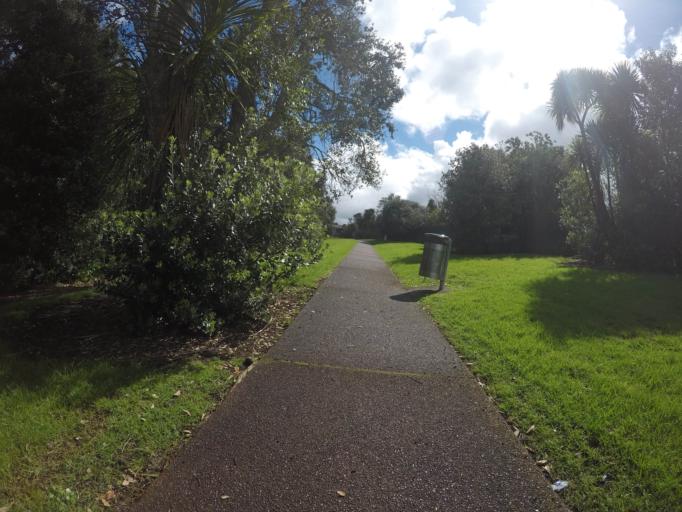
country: NZ
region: Auckland
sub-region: Auckland
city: Rosebank
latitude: -36.8968
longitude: 174.6775
